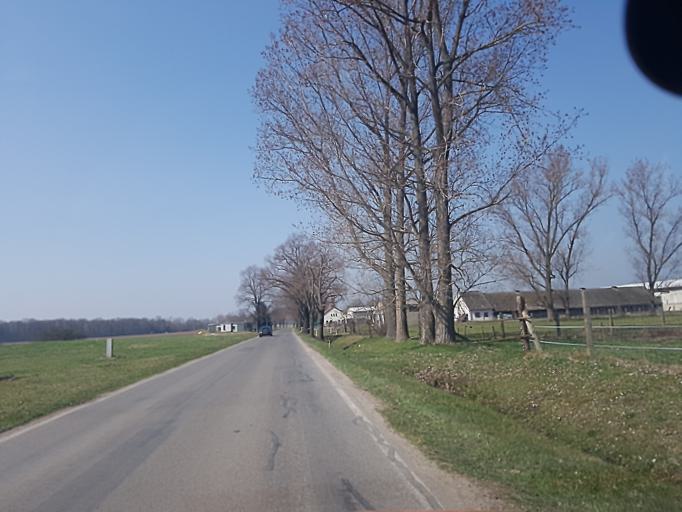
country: DE
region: Brandenburg
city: Forst
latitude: 51.6807
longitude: 14.5539
